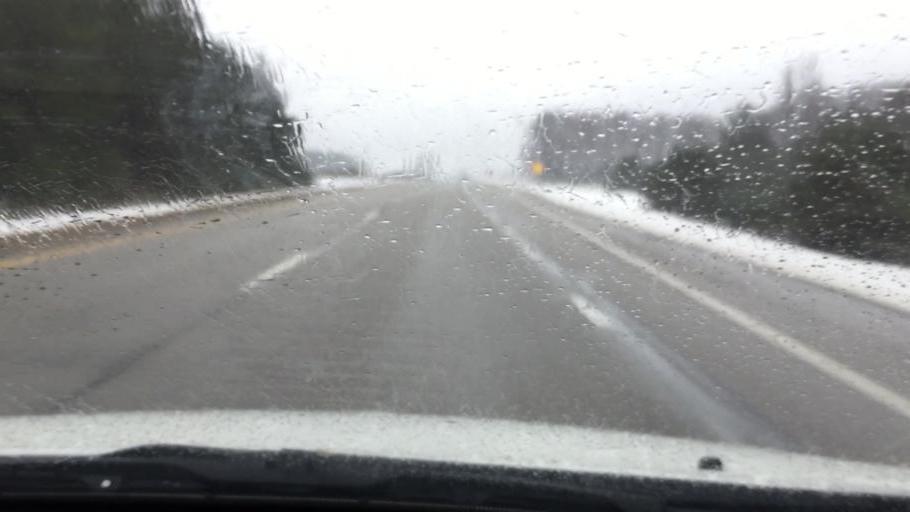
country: US
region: Michigan
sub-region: Wexford County
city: Cadillac
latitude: 44.1279
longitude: -85.4689
